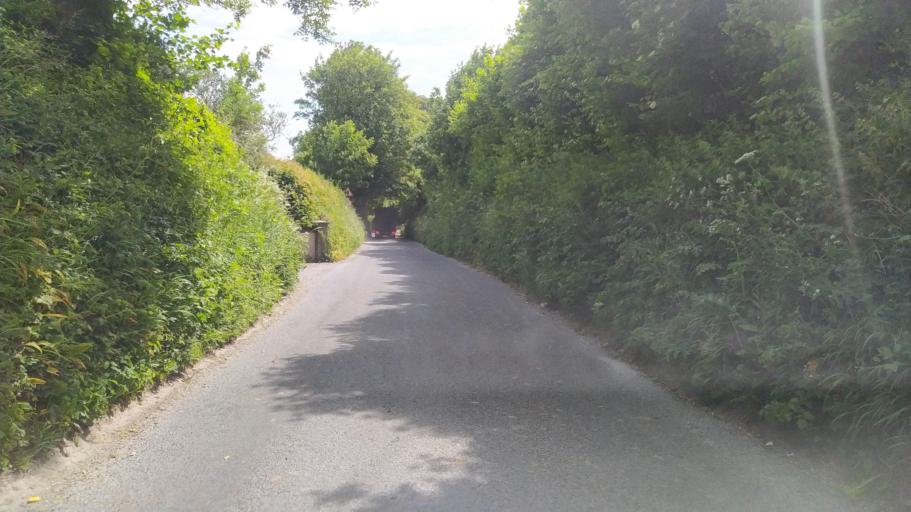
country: GB
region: England
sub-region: Dorset
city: Dorchester
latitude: 50.8076
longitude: -2.4855
